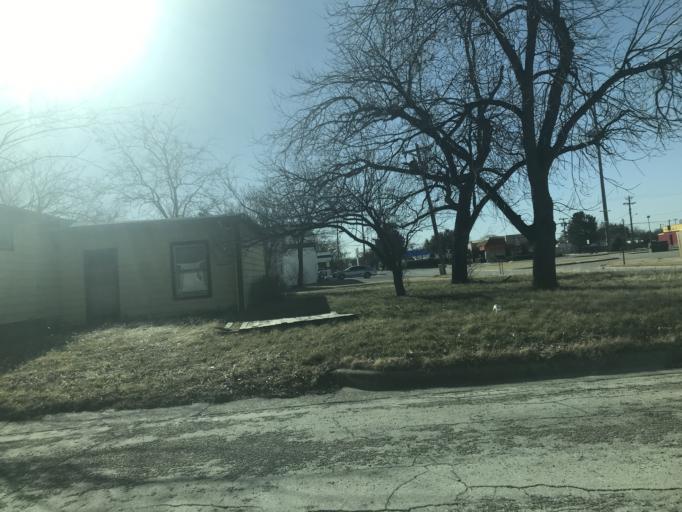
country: US
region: Texas
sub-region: Taylor County
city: Abilene
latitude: 32.4331
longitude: -99.7569
